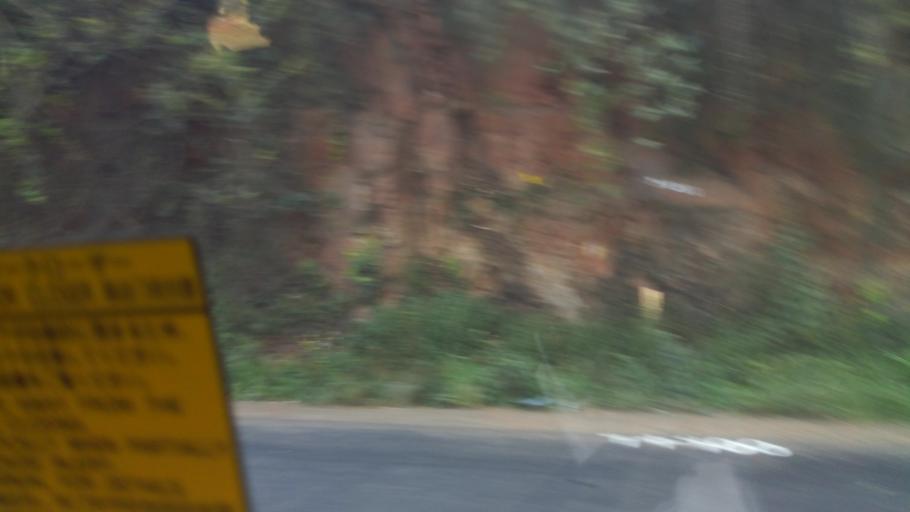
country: KE
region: Kiambu
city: Limuru
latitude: -1.0588
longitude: 36.6034
